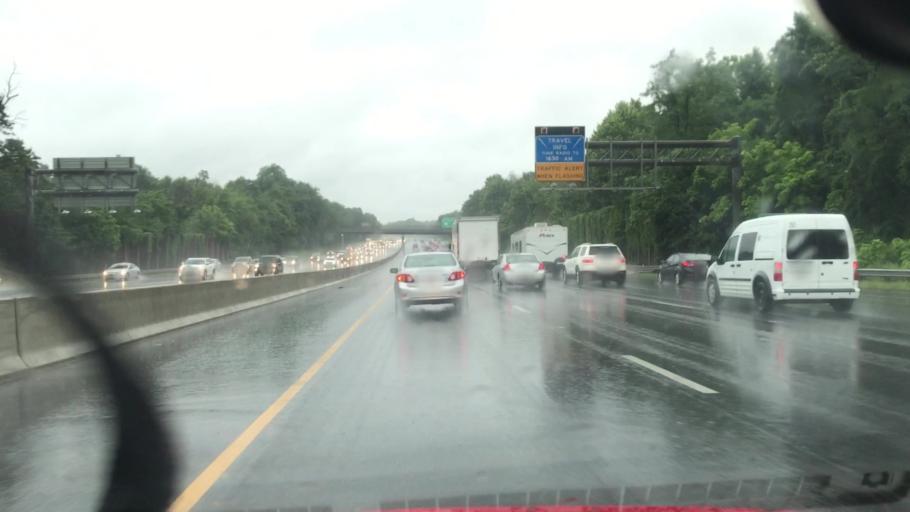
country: US
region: Maryland
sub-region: Prince George's County
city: Glenarden
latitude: 38.9341
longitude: -76.8550
